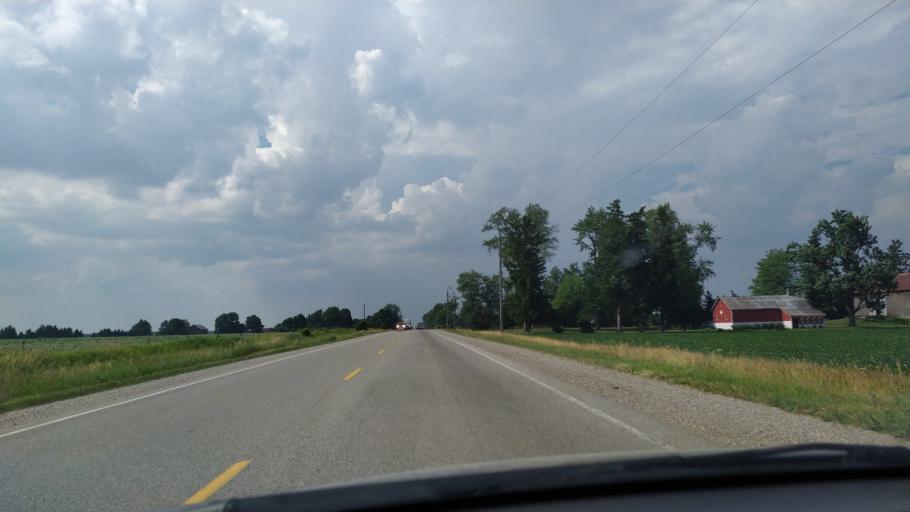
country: CA
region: Ontario
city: Dorchester
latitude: 43.0336
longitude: -81.1222
